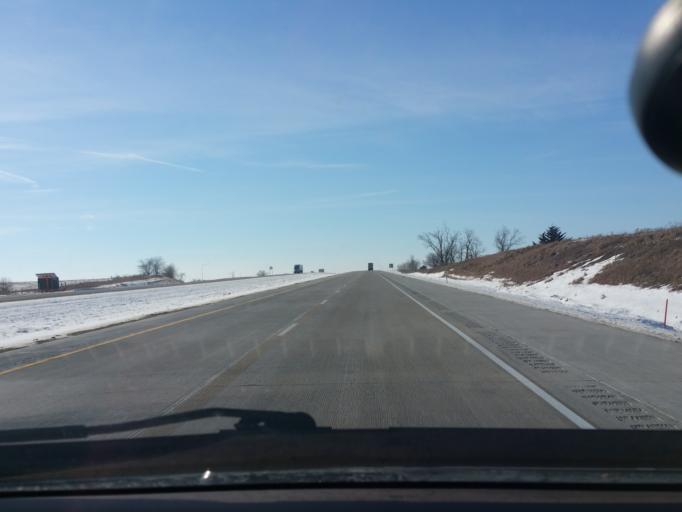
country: US
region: Iowa
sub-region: Decatur County
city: Lamoni
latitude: 40.5798
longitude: -93.9328
